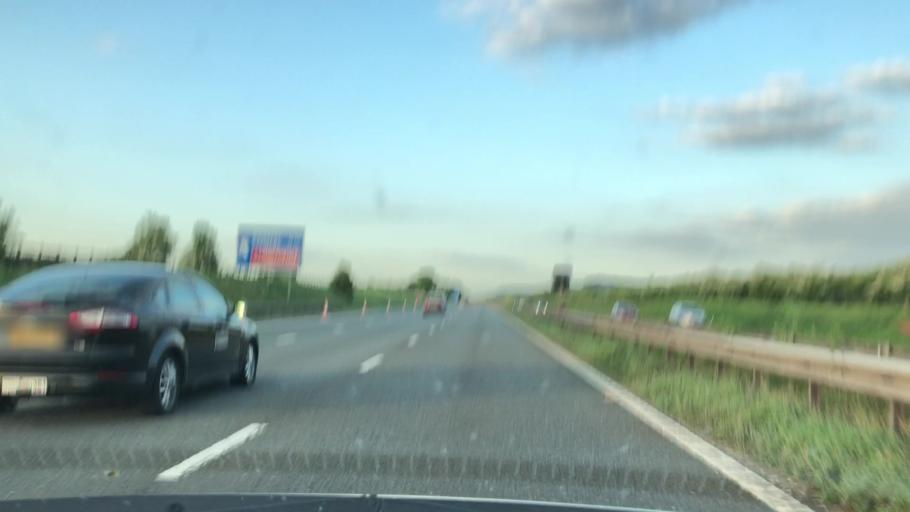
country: GB
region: England
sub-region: Cheshire West and Chester
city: Elton
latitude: 53.2627
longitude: -2.8164
